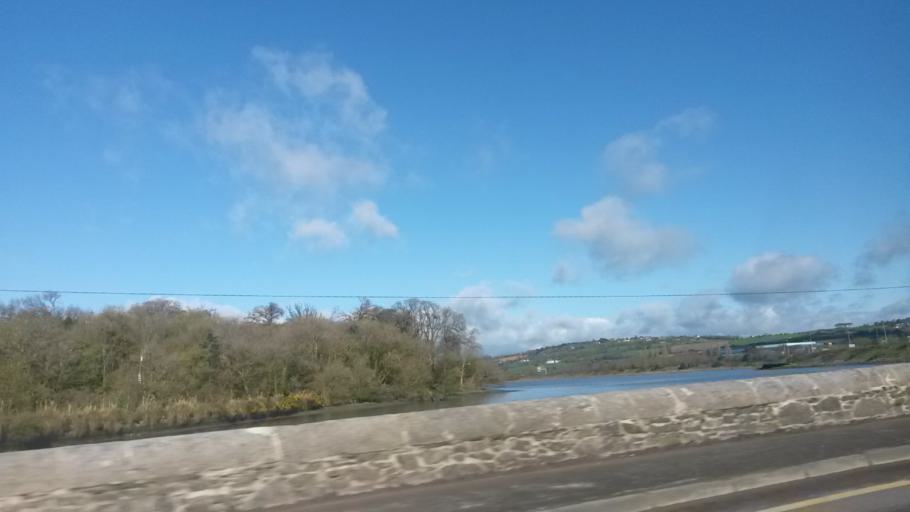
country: IE
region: Munster
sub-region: County Cork
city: Carrigtwohill
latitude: 51.9018
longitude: -8.2813
